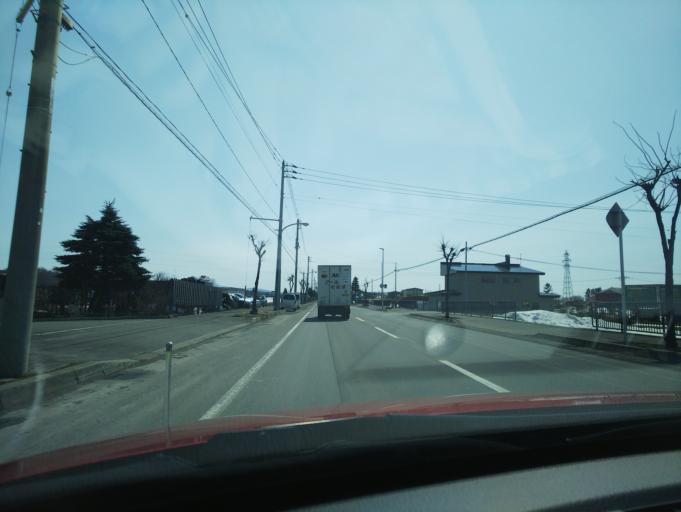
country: JP
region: Hokkaido
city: Nayoro
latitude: 44.3359
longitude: 142.4643
